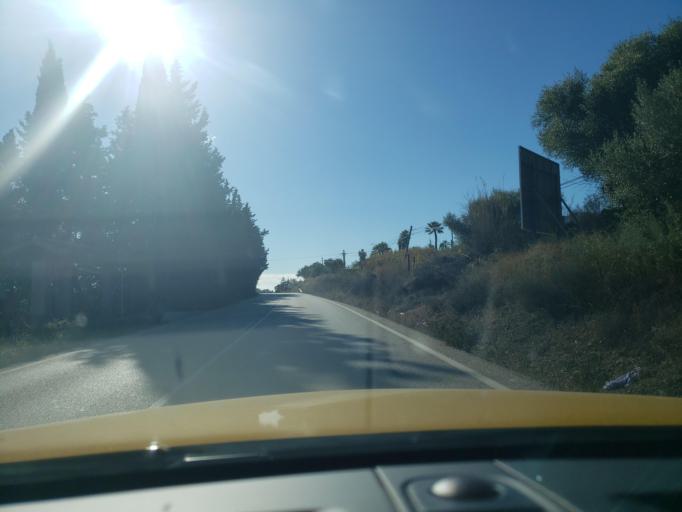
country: ES
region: Andalusia
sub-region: Provincia de Malaga
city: Benahavis
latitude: 36.4790
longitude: -5.0139
